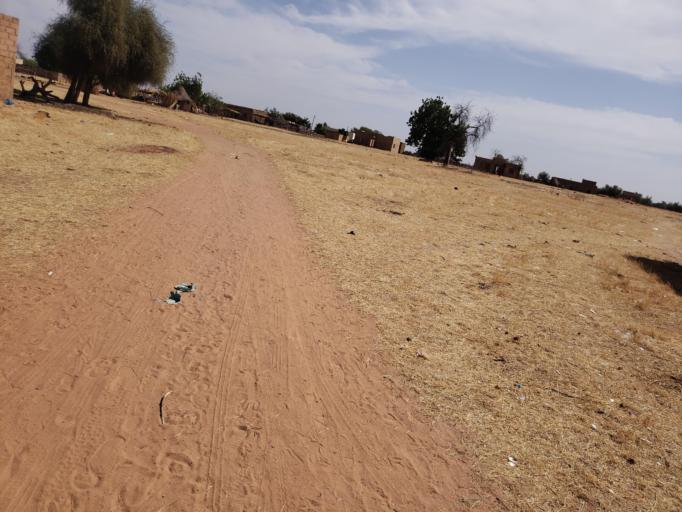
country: SN
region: Matam
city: Ranerou
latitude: 15.2985
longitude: -13.9669
